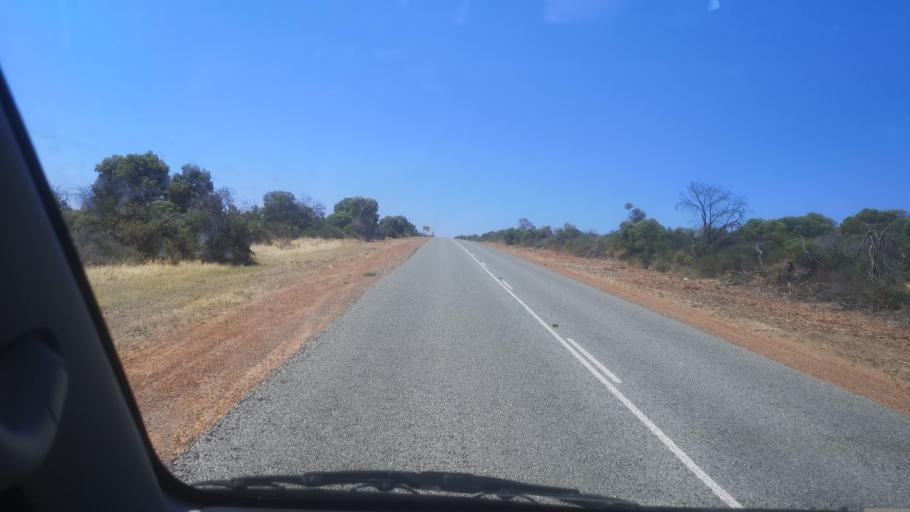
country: AU
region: Western Australia
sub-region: Northampton Shire
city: Kalbarri
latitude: -28.0515
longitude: 114.1914
